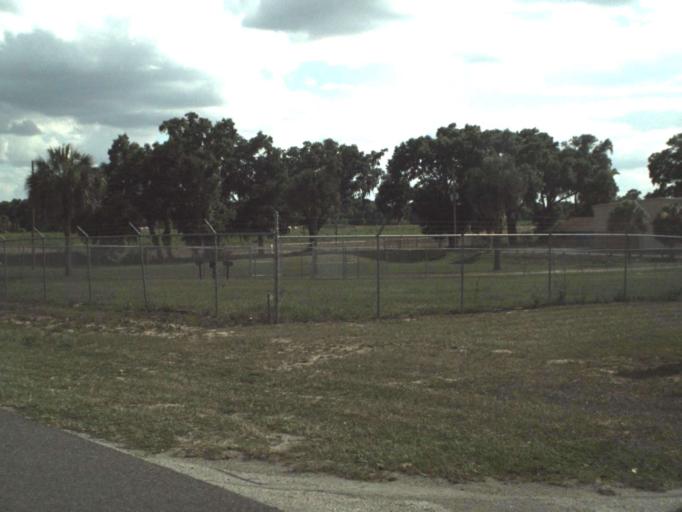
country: US
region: Florida
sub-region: Marion County
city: Belleview
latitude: 29.0816
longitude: -82.0536
